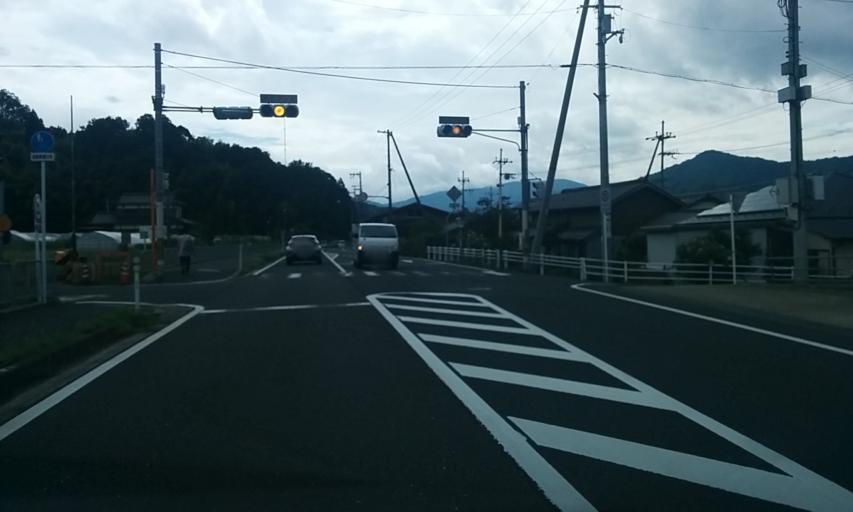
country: JP
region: Kyoto
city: Miyazu
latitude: 35.5418
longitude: 135.2089
